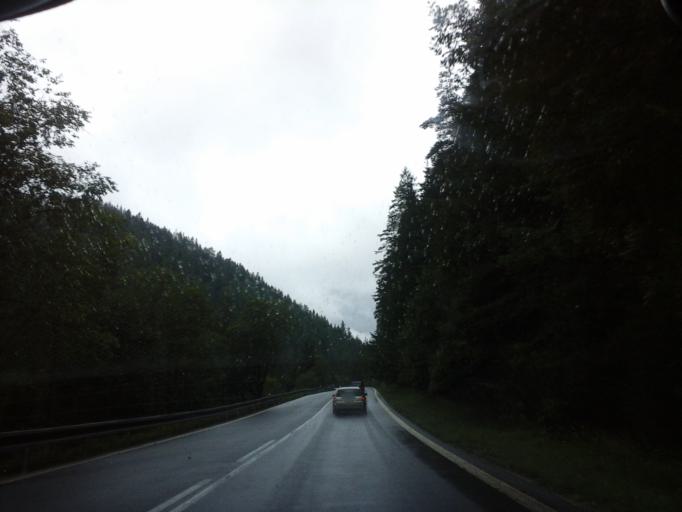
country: SK
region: Kosicky
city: Dobsina
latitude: 48.8743
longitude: 20.2679
